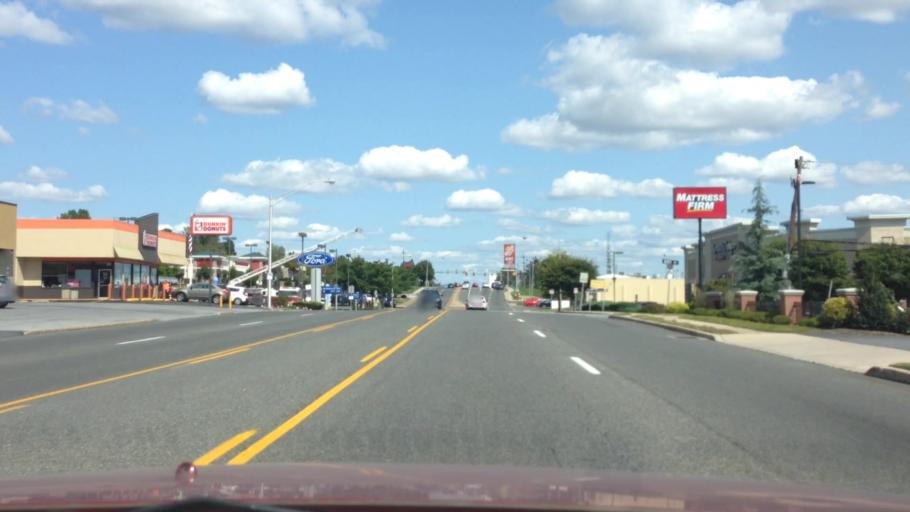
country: US
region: Pennsylvania
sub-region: Delaware County
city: Springfield
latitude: 39.9235
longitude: -75.3148
